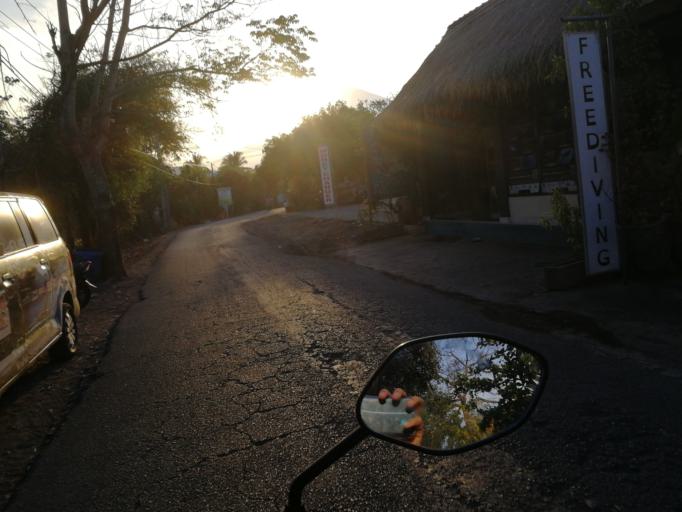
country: ID
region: Bali
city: Biaslantang Kaler
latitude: -8.3353
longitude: 115.6530
